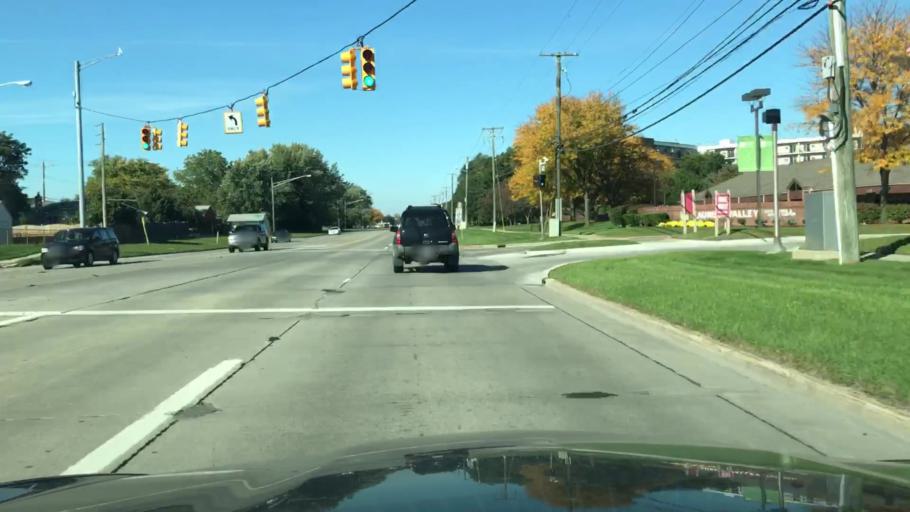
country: US
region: Michigan
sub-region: Macomb County
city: Sterling Heights
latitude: 42.5573
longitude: -83.0884
